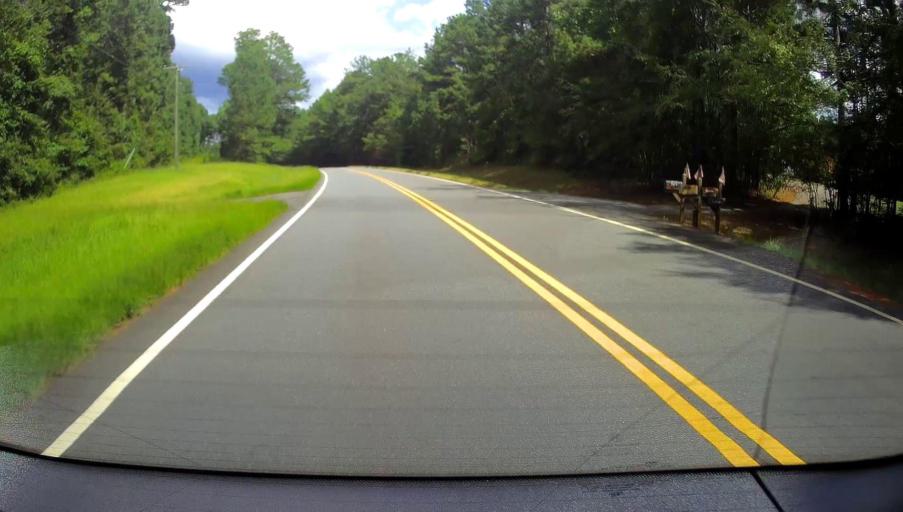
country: US
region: Georgia
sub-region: Crawford County
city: Knoxville
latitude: 32.8730
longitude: -83.9866
